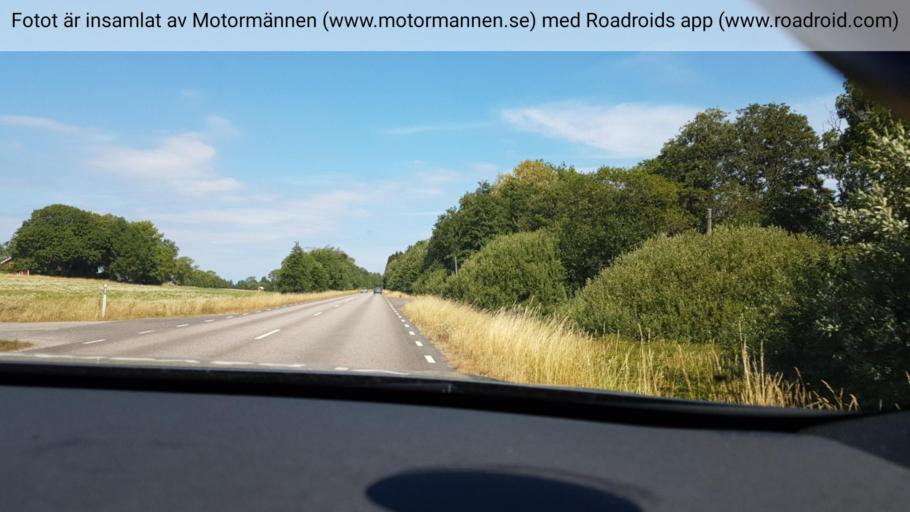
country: SE
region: Vaestra Goetaland
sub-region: Gotene Kommun
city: Kallby
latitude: 58.5870
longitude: 13.3776
